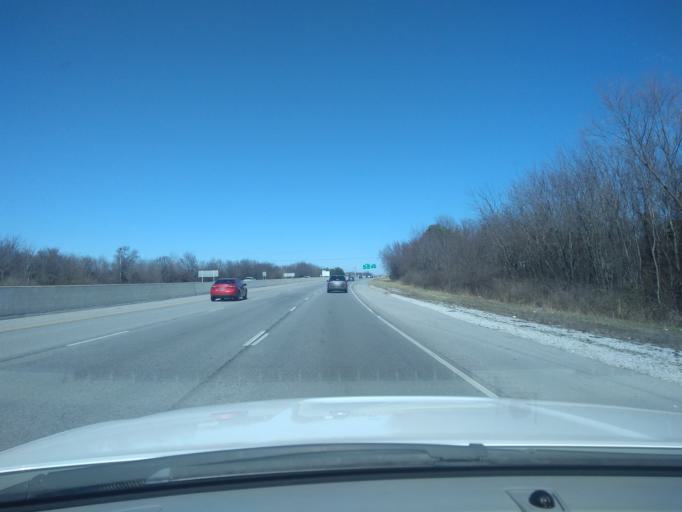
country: US
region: Arkansas
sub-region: Washington County
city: Fayetteville
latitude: 36.0839
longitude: -94.1976
